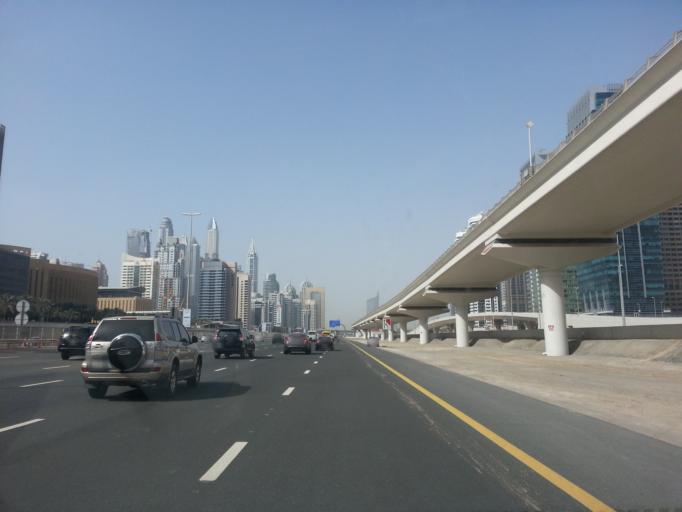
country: AE
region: Dubai
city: Dubai
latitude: 25.0725
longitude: 55.1399
